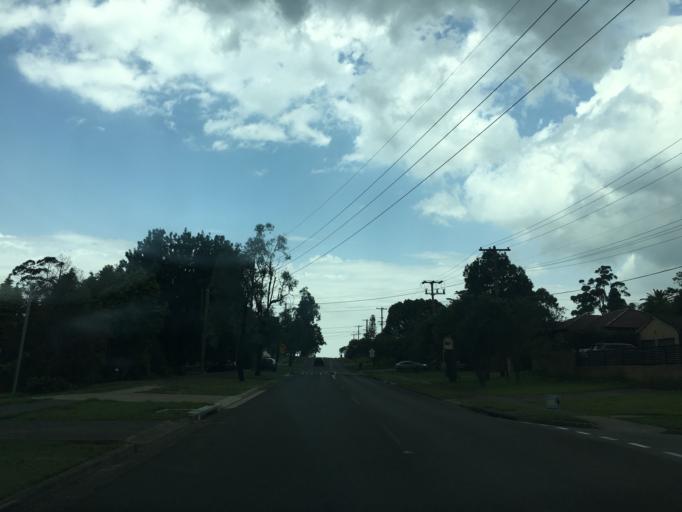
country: AU
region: New South Wales
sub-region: Ryde
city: Marsfield
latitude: -33.7909
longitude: 151.1057
